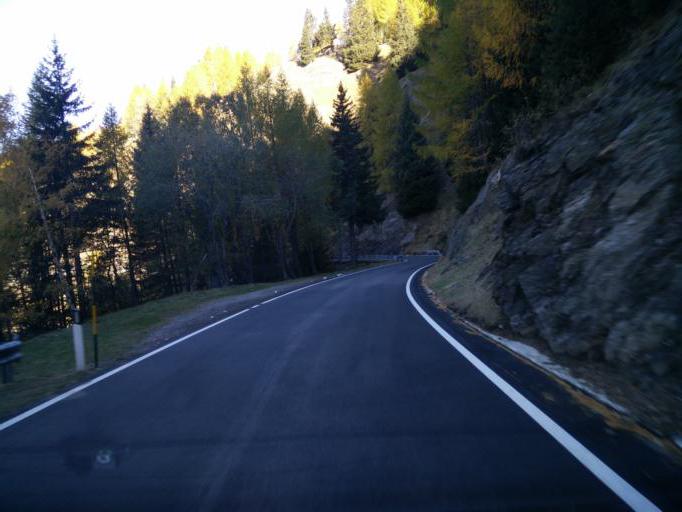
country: IT
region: Trentino-Alto Adige
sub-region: Bolzano
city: Moso in Passiria
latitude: 46.8814
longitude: 11.1510
